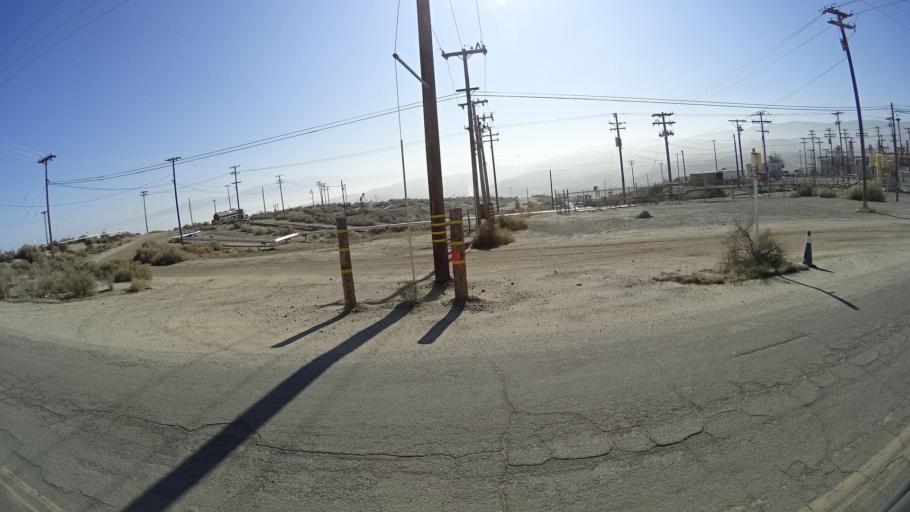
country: US
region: California
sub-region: Kern County
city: Taft Heights
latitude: 35.1145
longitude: -119.4694
